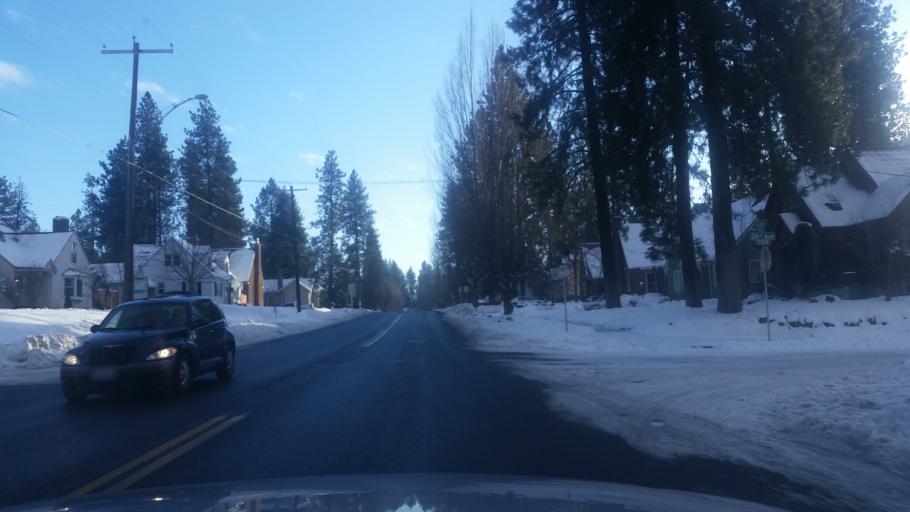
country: US
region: Washington
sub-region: Spokane County
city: Spokane
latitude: 47.6312
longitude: -117.4250
